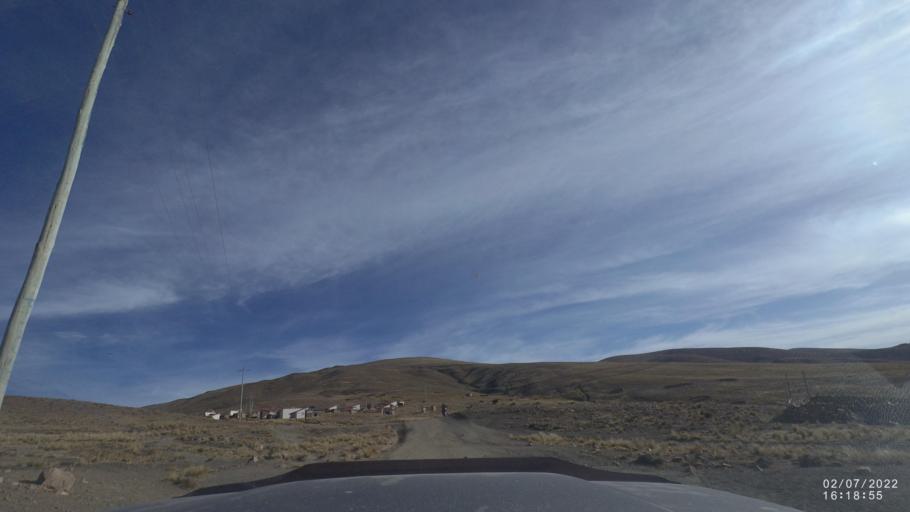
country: BO
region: Cochabamba
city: Irpa Irpa
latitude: -17.9281
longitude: -66.4430
